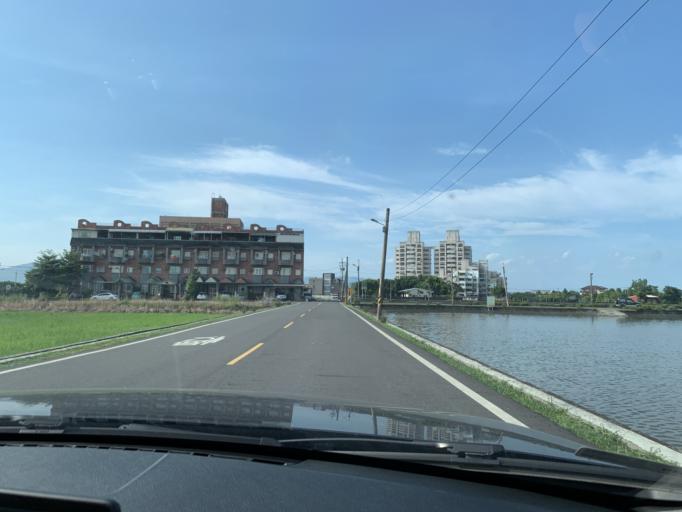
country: TW
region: Taiwan
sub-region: Yilan
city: Yilan
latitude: 24.6774
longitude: 121.8099
